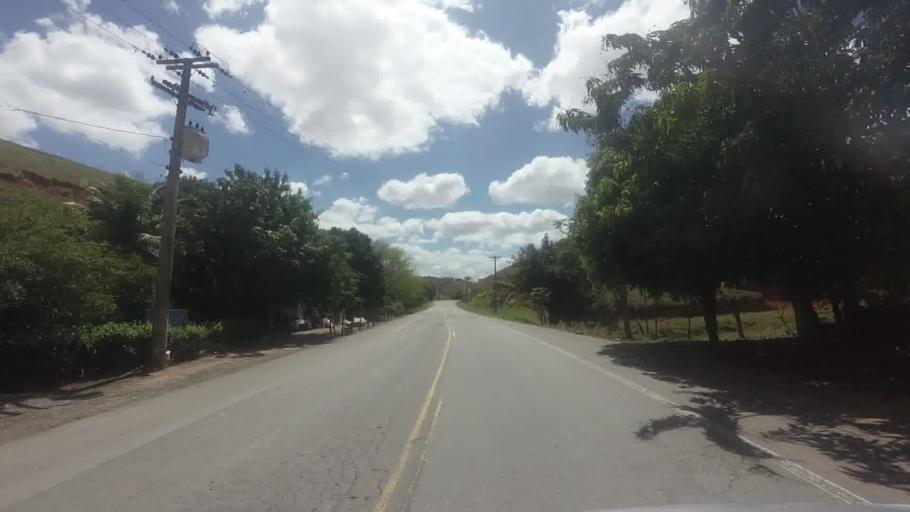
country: BR
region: Rio de Janeiro
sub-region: Santo Antonio De Padua
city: Santo Antonio de Padua
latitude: -21.6535
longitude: -42.2976
